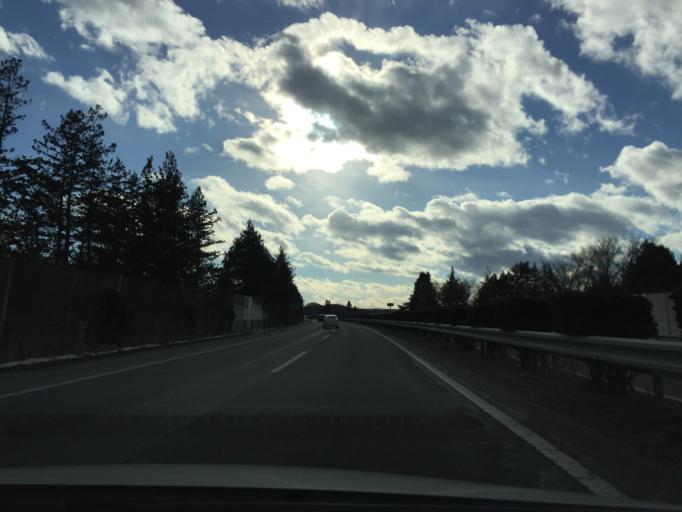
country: JP
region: Tochigi
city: Kuroiso
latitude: 37.1320
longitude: 140.1820
